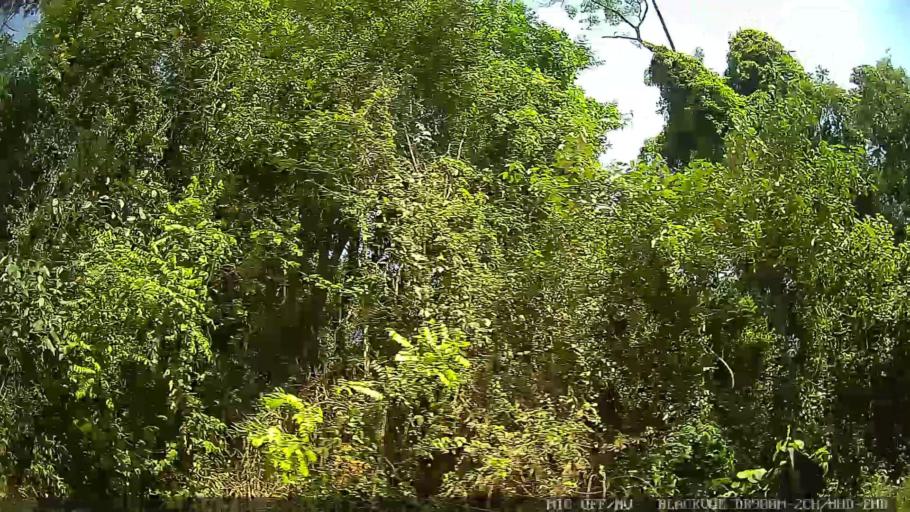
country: BR
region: Sao Paulo
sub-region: Vinhedo
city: Vinhedo
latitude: -23.0200
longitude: -46.9272
